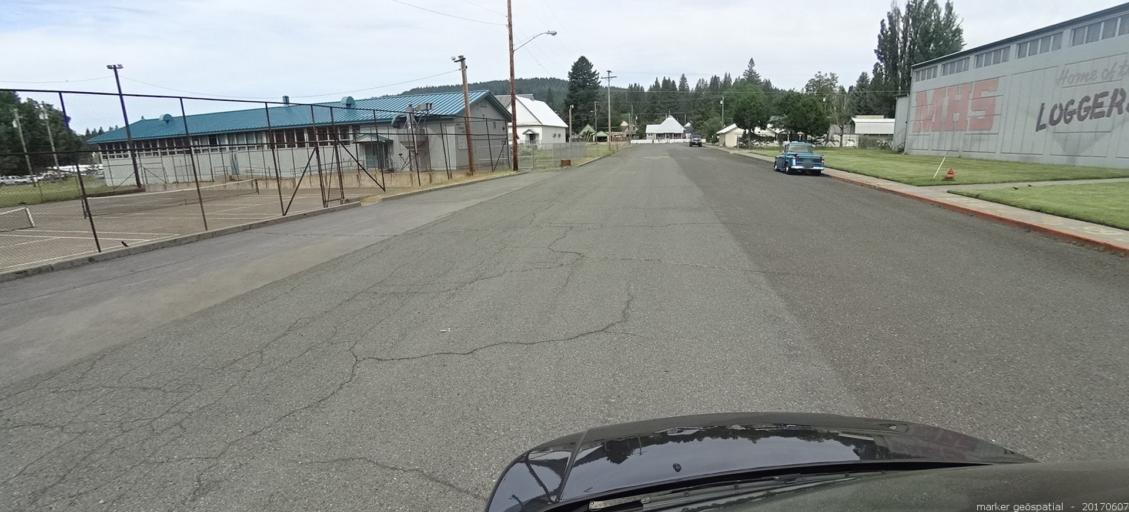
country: US
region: California
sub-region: Siskiyou County
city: McCloud
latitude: 41.2538
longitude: -122.1343
